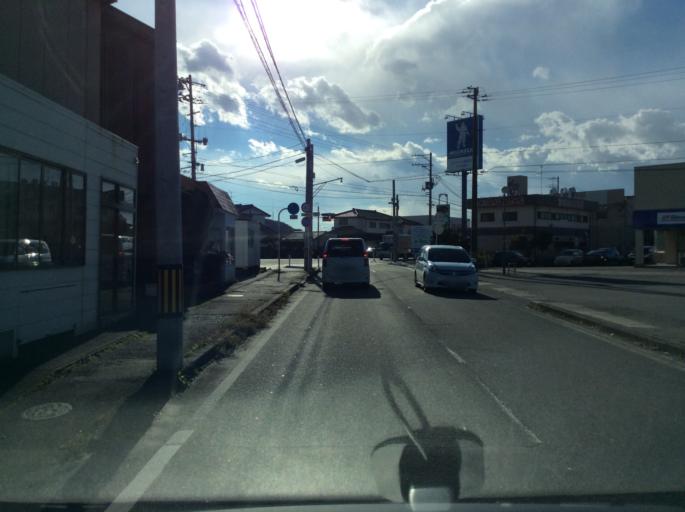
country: JP
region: Fukushima
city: Iwaki
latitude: 37.0603
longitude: 140.9240
